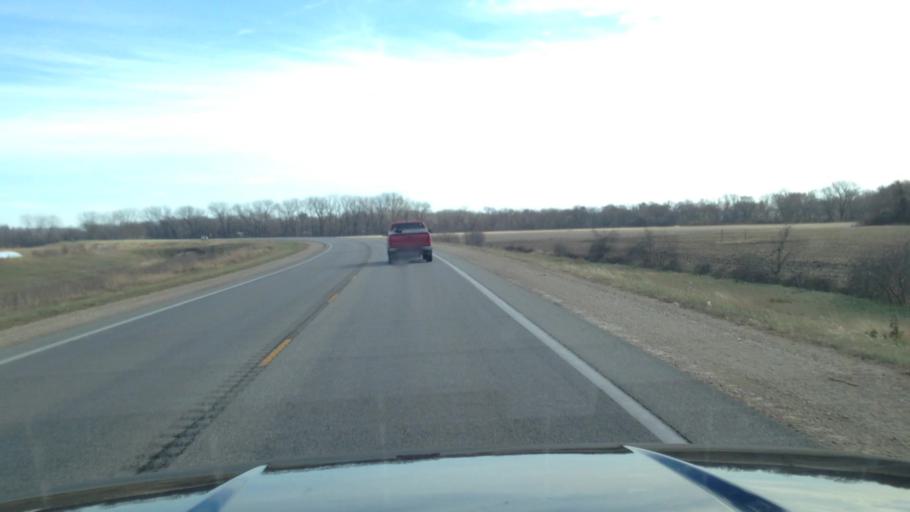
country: US
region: Kansas
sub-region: Jefferson County
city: Oskaloosa
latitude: 39.0825
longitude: -95.4062
